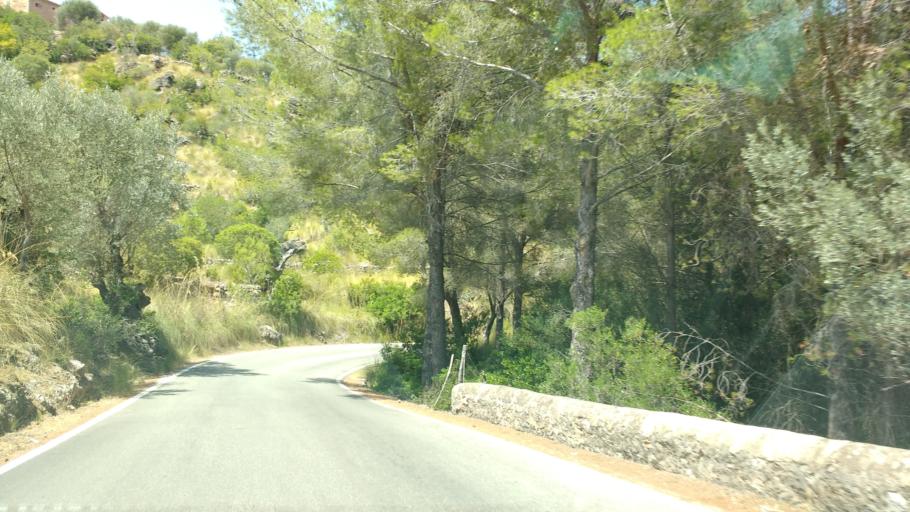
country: ES
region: Balearic Islands
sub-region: Illes Balears
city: Escorca
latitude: 39.8430
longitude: 2.7958
